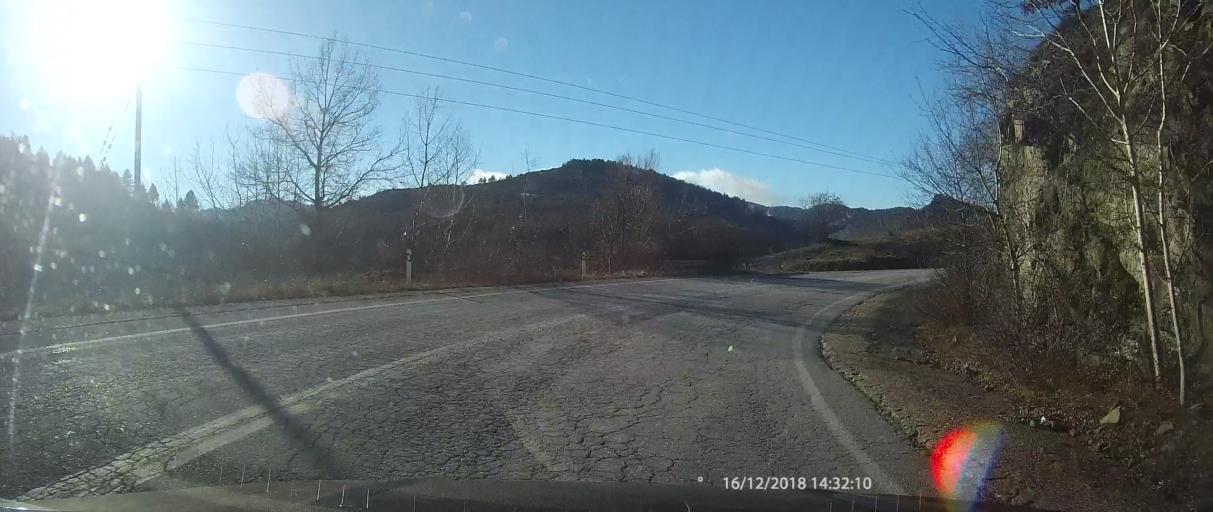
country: GR
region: West Macedonia
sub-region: Nomos Kozanis
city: Tsotili
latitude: 40.1948
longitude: 21.1730
